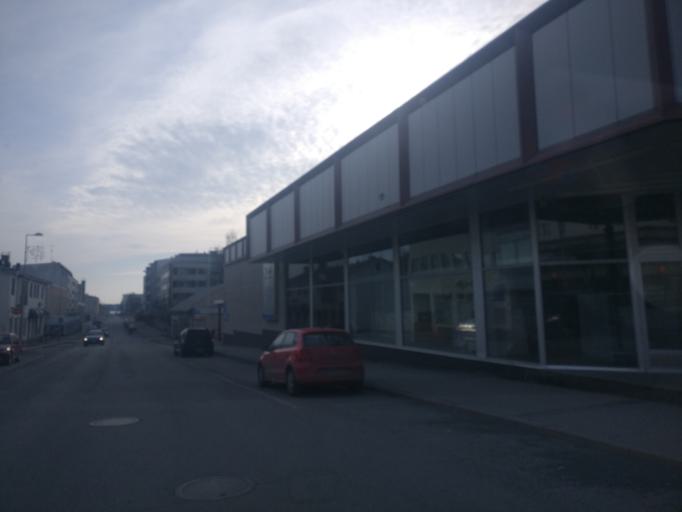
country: FI
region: Lapland
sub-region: Kemi-Tornio
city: Kemi
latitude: 65.7370
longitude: 24.5661
